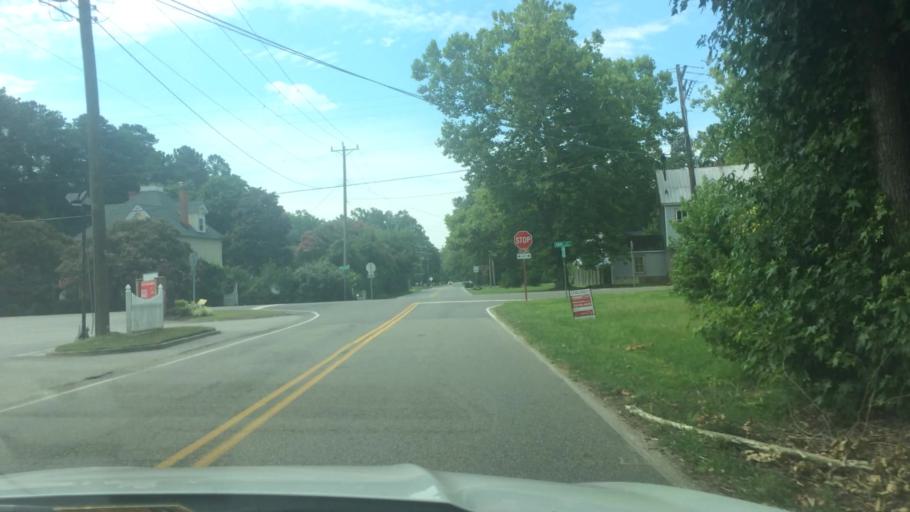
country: US
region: Virginia
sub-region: York County
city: Yorktown
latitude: 37.1696
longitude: -76.4385
